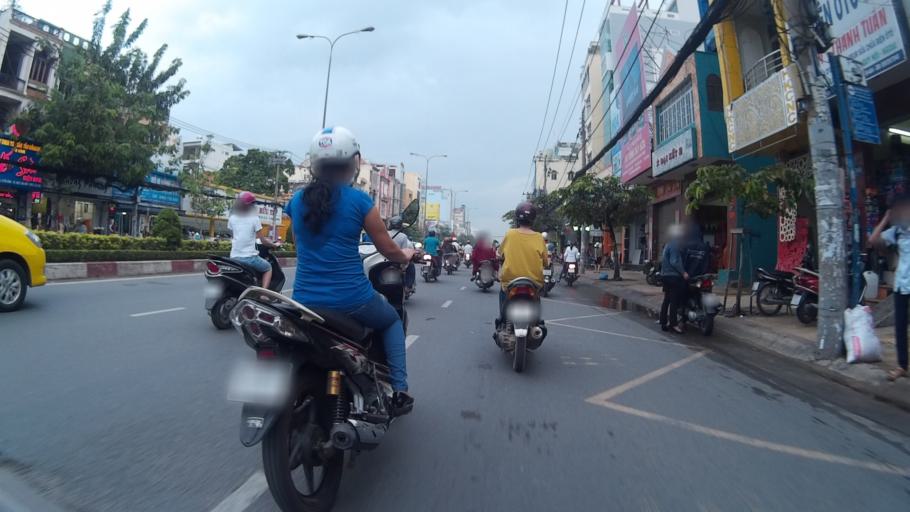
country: VN
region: Ho Chi Minh City
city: Quan Tan Phu
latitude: 10.8021
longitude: 106.6436
